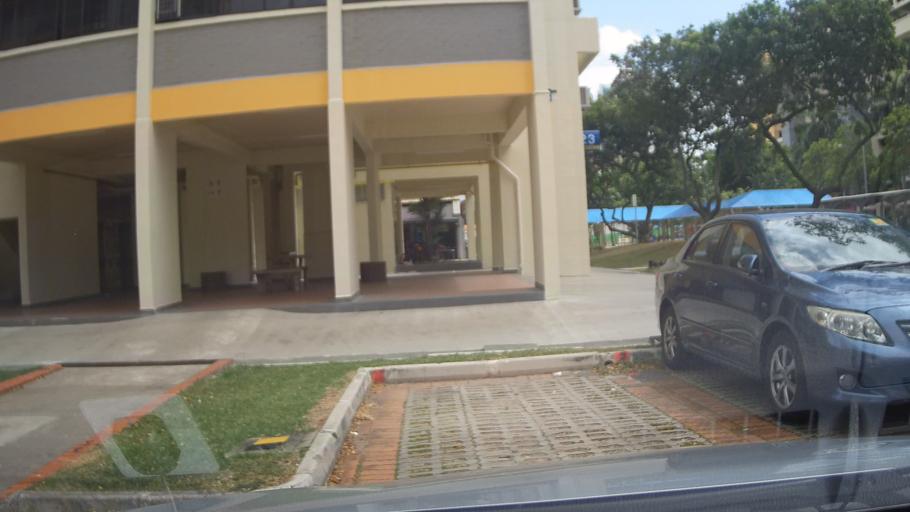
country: SG
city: Singapore
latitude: 1.3033
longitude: 103.7632
